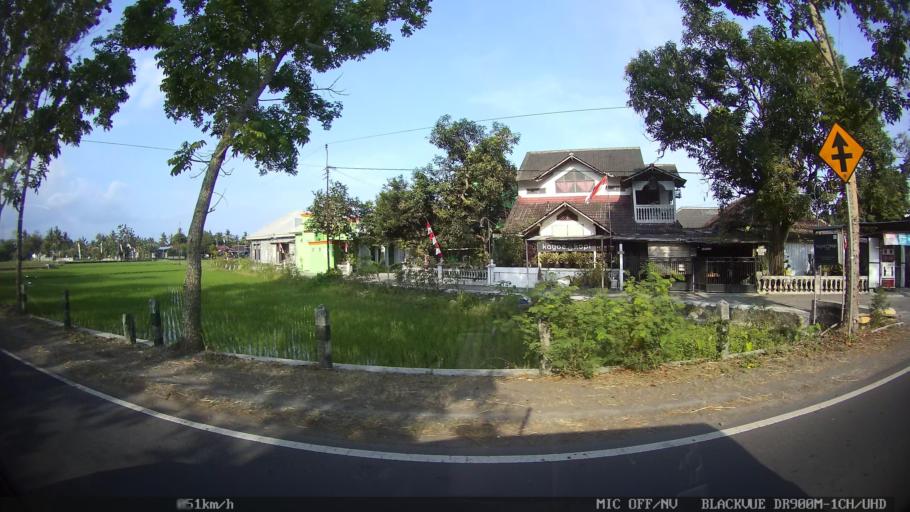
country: ID
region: Daerah Istimewa Yogyakarta
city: Bantul
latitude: -7.8829
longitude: 110.3193
